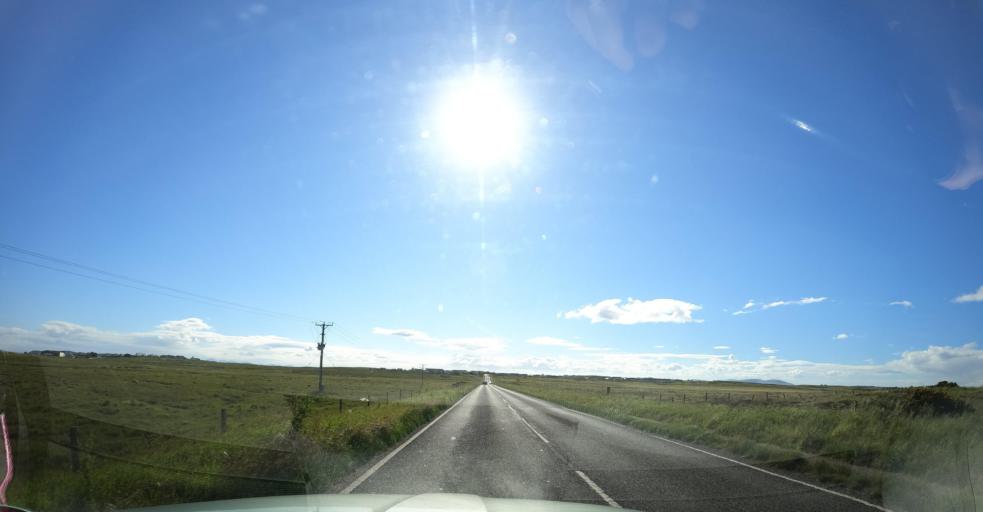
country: GB
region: Scotland
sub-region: Eilean Siar
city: Stornoway
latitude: 58.2038
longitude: -6.3221
